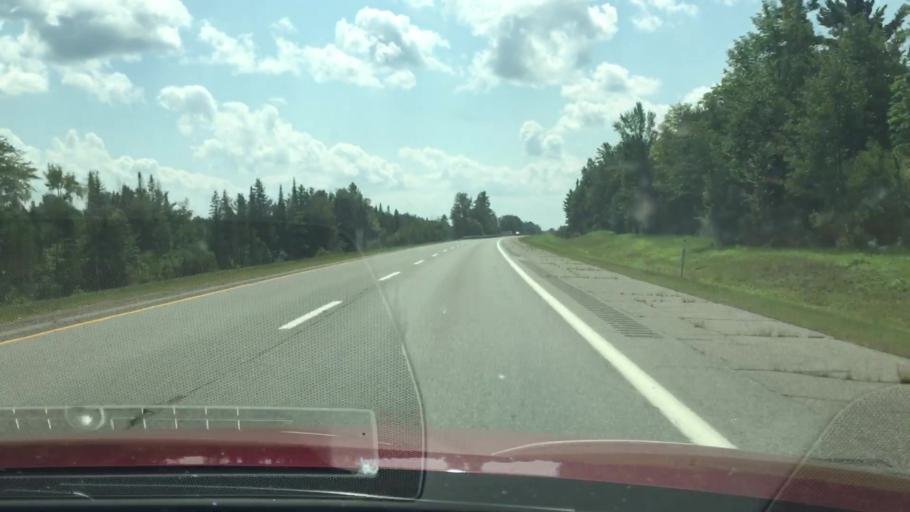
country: US
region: Maine
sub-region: Penobscot County
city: Medway
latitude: 45.5040
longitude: -68.5567
